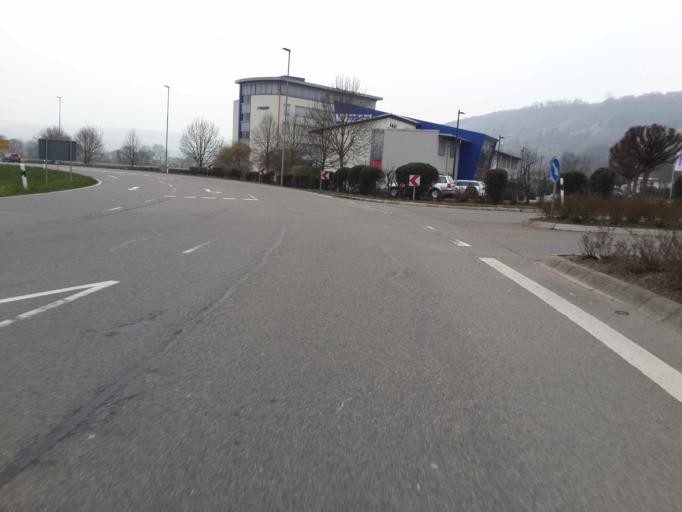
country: DE
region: Baden-Wuerttemberg
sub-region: Karlsruhe Region
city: Obrigheim
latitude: 49.3532
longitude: 9.1052
